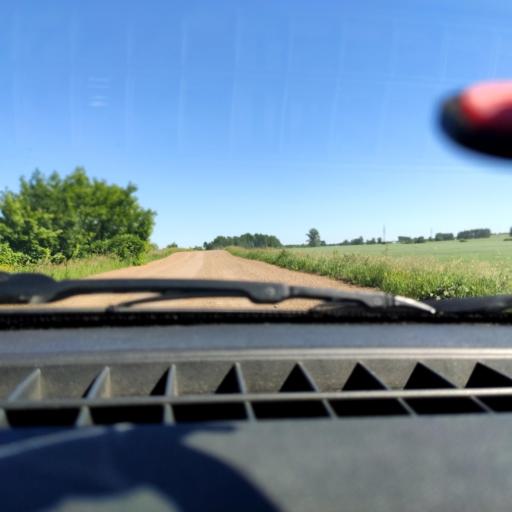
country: RU
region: Bashkortostan
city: Iglino
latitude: 54.9067
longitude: 56.4786
